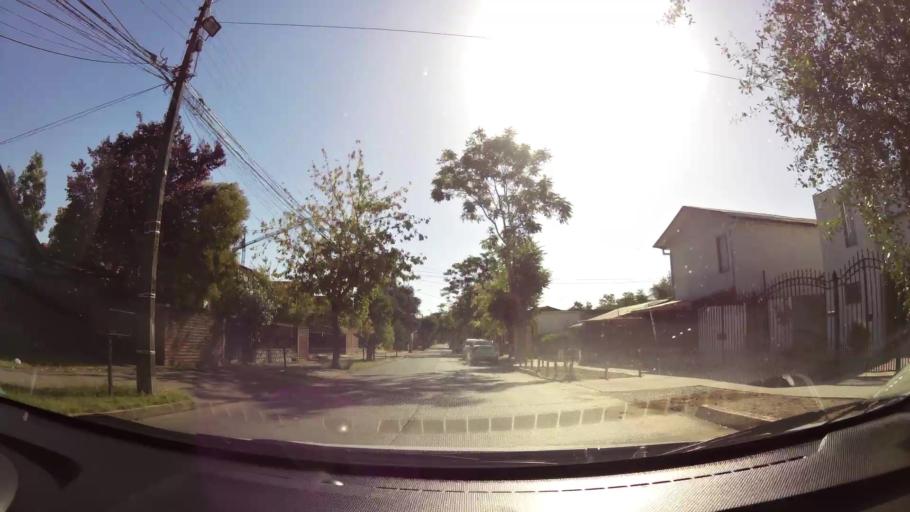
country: CL
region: Maule
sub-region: Provincia de Talca
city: Talca
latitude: -35.4267
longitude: -71.6719
